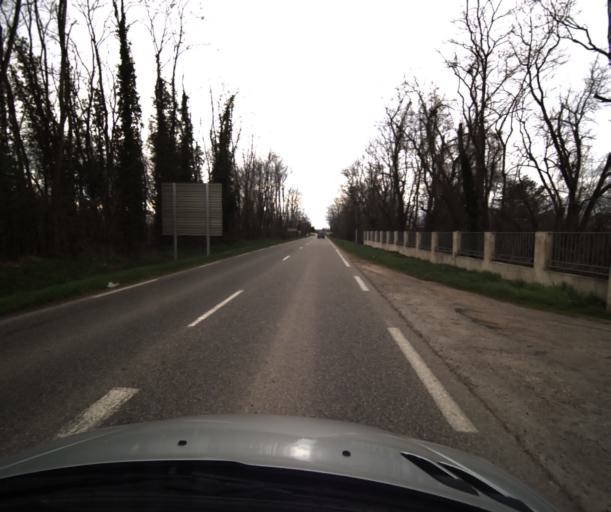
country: FR
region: Midi-Pyrenees
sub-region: Departement du Tarn-et-Garonne
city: Montricoux
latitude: 44.0736
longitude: 1.6118
